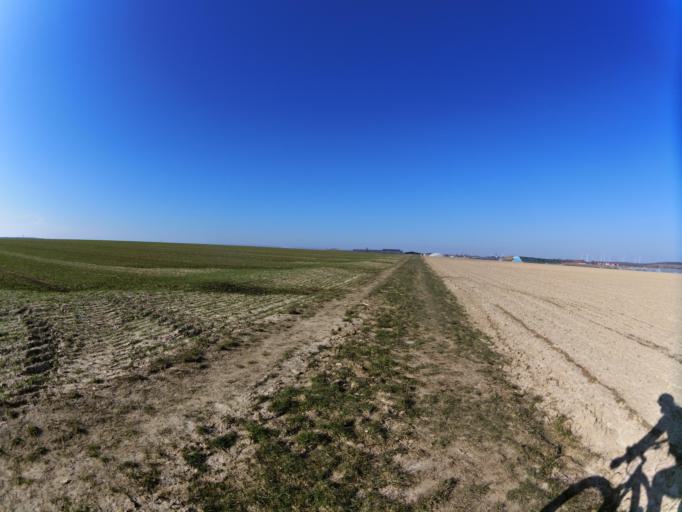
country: DE
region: Bavaria
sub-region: Regierungsbezirk Unterfranken
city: Bergtheim
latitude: 49.8824
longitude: 10.0623
